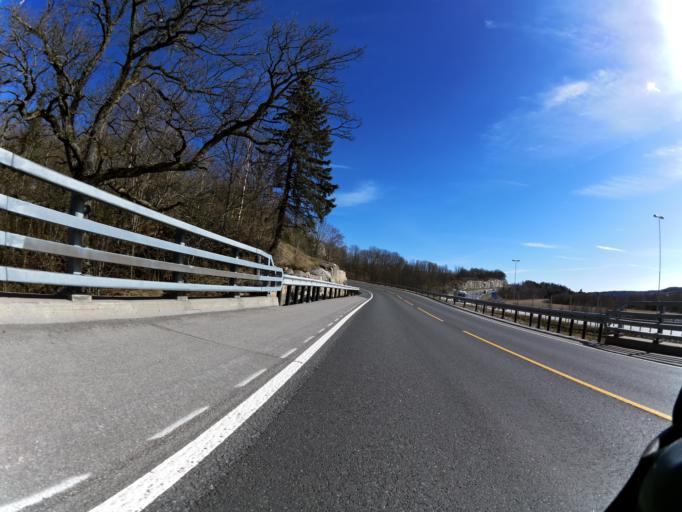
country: NO
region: Ostfold
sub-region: Rade
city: Karlshus
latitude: 59.3249
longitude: 10.9620
